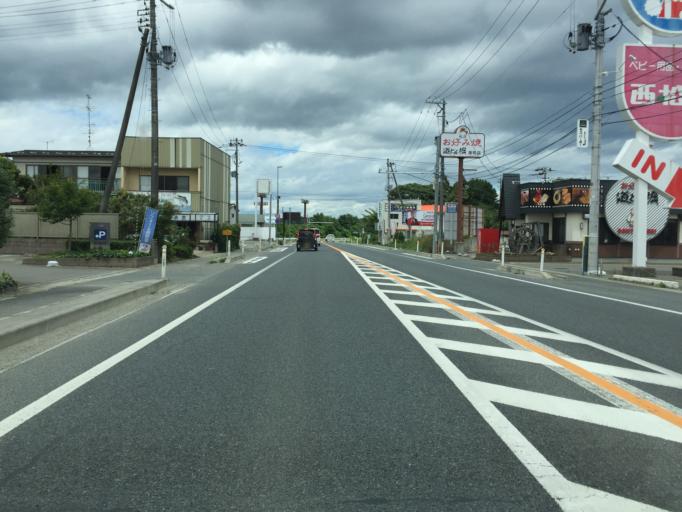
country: JP
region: Fukushima
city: Namie
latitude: 37.6391
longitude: 140.9835
